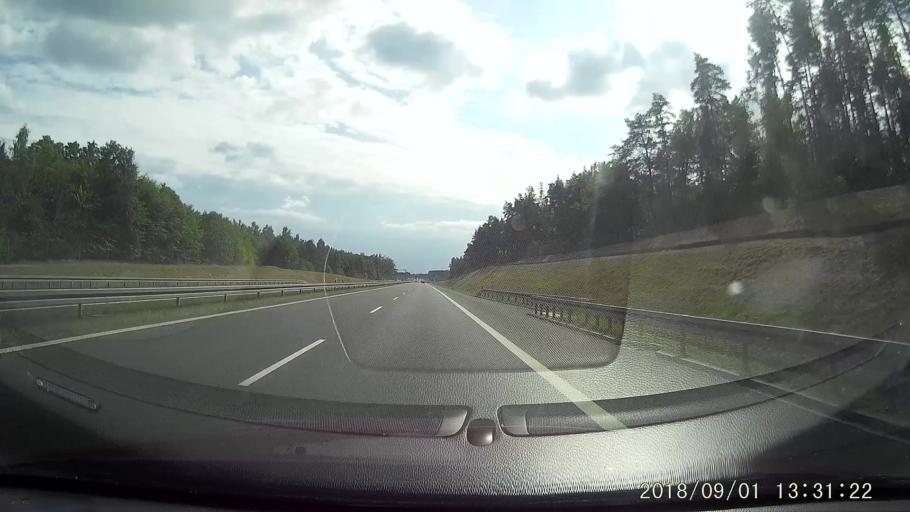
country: PL
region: West Pomeranian Voivodeship
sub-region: Powiat mysliborski
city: Mysliborz
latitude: 53.0182
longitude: 14.8614
